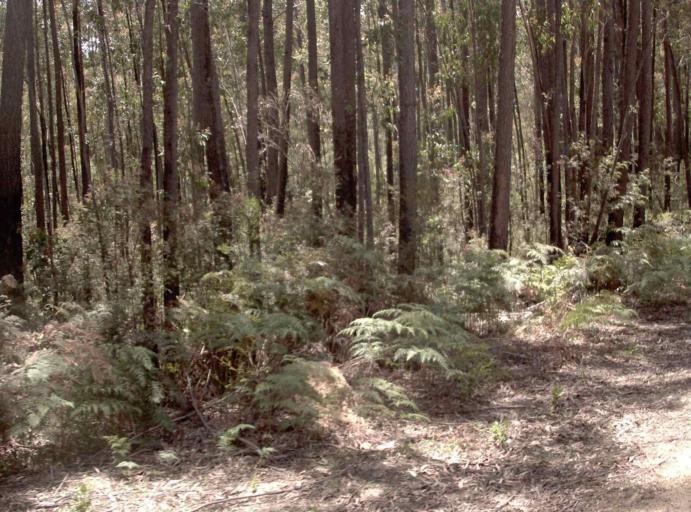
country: AU
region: New South Wales
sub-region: Bombala
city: Bombala
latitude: -37.5702
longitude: 148.9434
